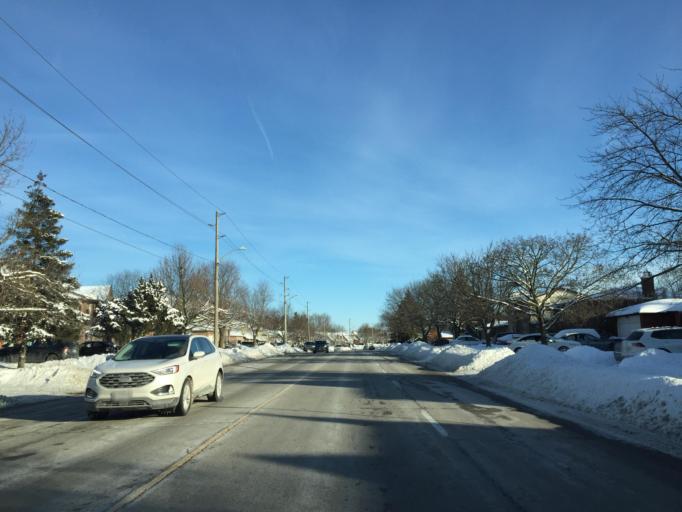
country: CA
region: Ontario
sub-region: Wellington County
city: Guelph
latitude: 43.5125
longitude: -80.2331
